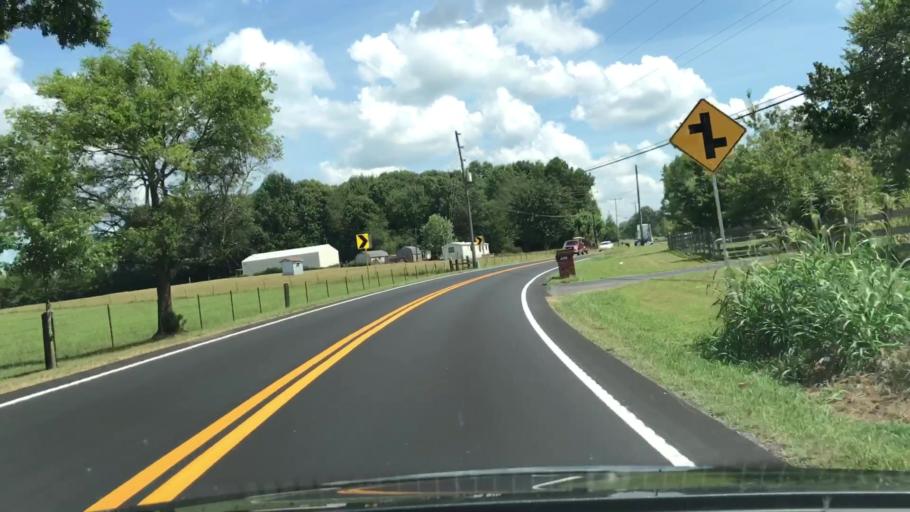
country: US
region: Tennessee
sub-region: Sumner County
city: White House
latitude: 36.4842
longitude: -86.6163
